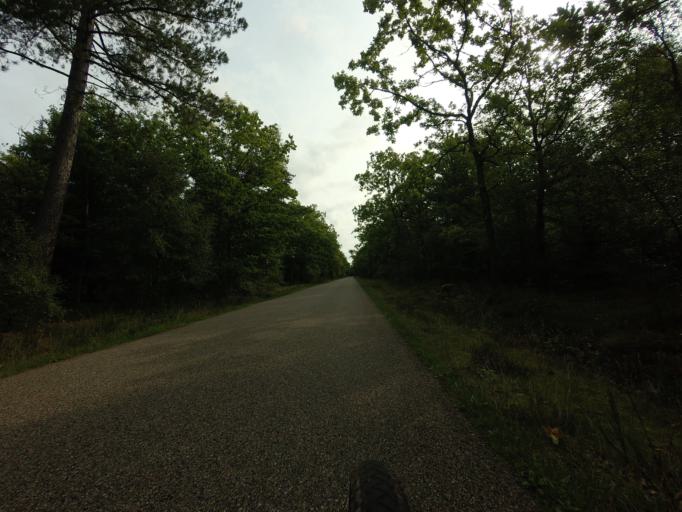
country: DK
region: North Denmark
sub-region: Hjorring Kommune
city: Hirtshals
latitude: 57.5792
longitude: 10.0983
